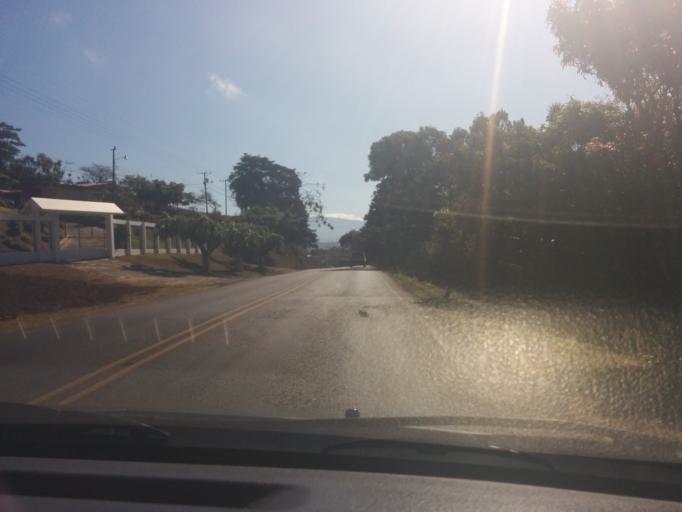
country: CR
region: Alajuela
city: San Rafael
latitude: 10.0722
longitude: -84.4847
